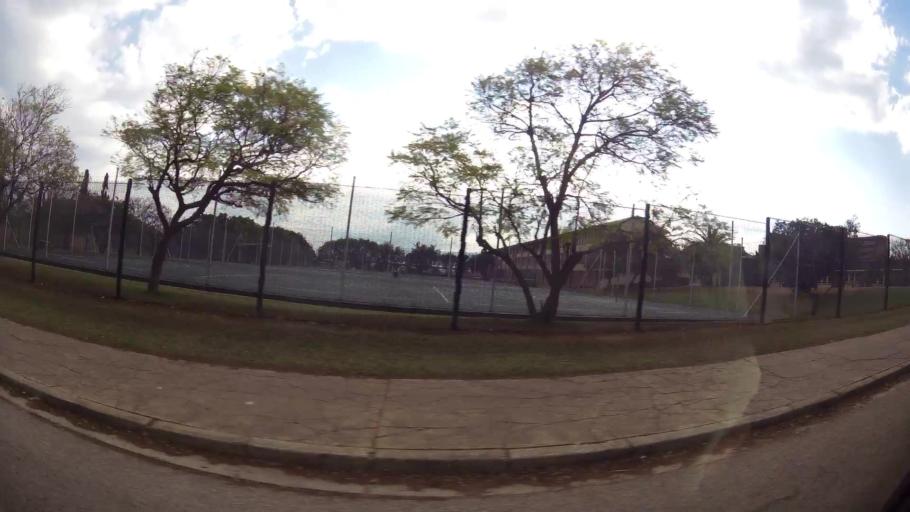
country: ZA
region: Eastern Cape
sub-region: Nelson Mandela Bay Metropolitan Municipality
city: Uitenhage
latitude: -33.7442
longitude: 25.4070
